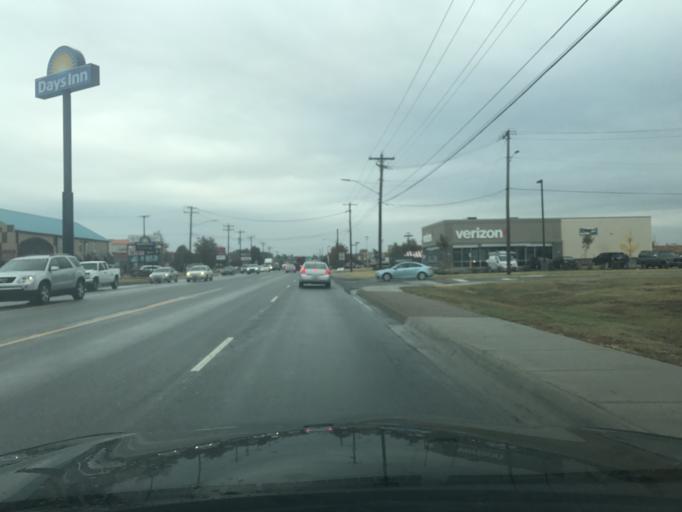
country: US
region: Arkansas
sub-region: Faulkner County
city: Conway
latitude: 35.0913
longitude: -92.4177
